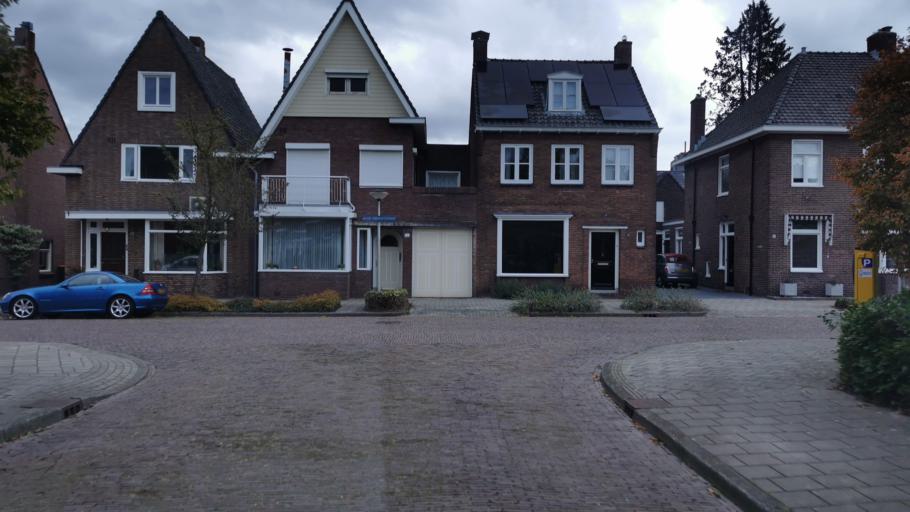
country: NL
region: Overijssel
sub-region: Gemeente Enschede
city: Enschede
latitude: 52.2110
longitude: 6.8973
